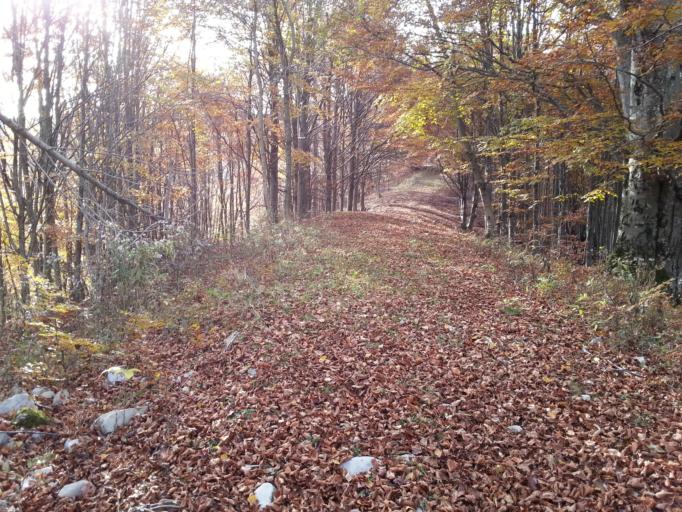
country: IT
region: Lombardy
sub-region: Provincia di Lecco
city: Morterone
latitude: 45.8750
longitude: 9.5024
